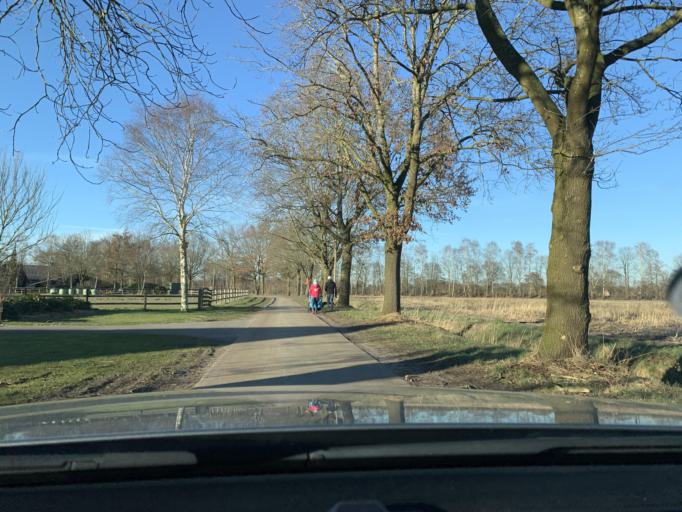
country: DE
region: Lower Saxony
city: Hatten
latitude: 53.1082
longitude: 8.3255
